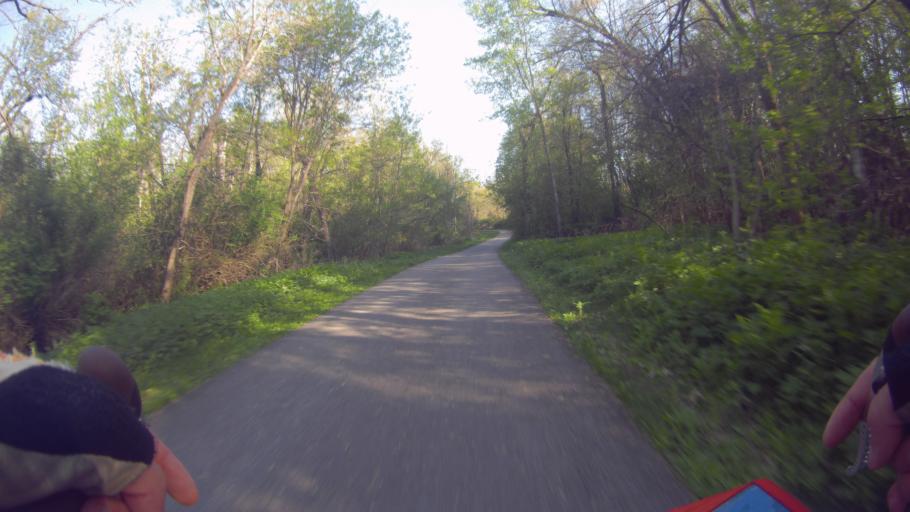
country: US
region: Wisconsin
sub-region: Dane County
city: Shorewood Hills
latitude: 43.0230
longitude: -89.4597
